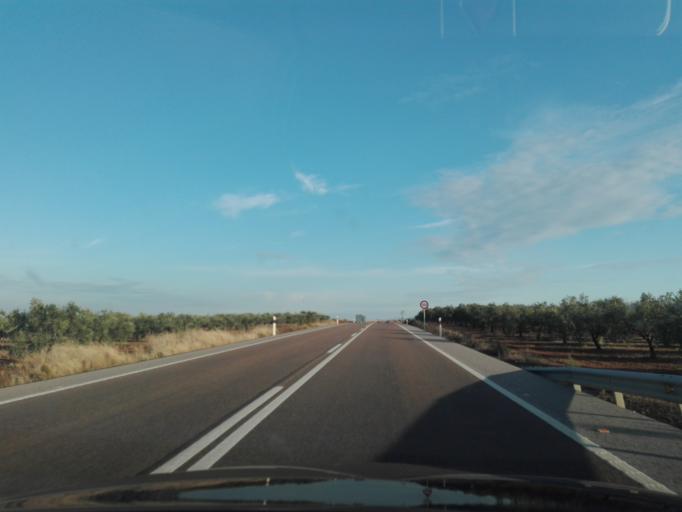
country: ES
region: Extremadura
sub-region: Provincia de Badajoz
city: Usagre
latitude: 38.3421
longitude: -6.1657
